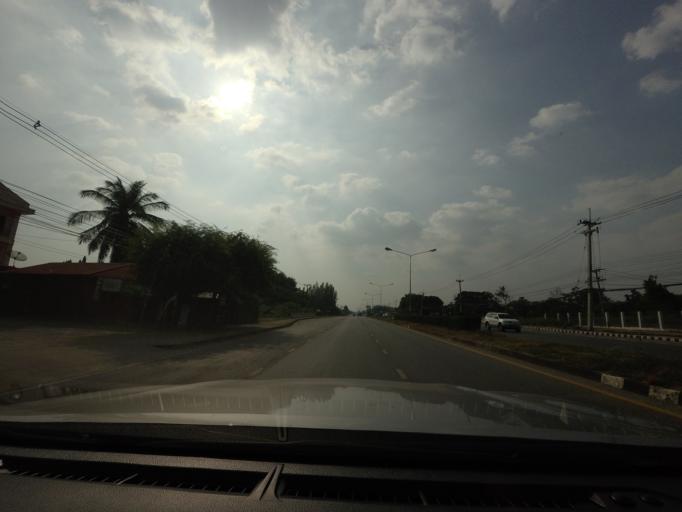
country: TH
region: Sukhothai
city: Sukhothai
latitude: 17.0179
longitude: 99.8559
